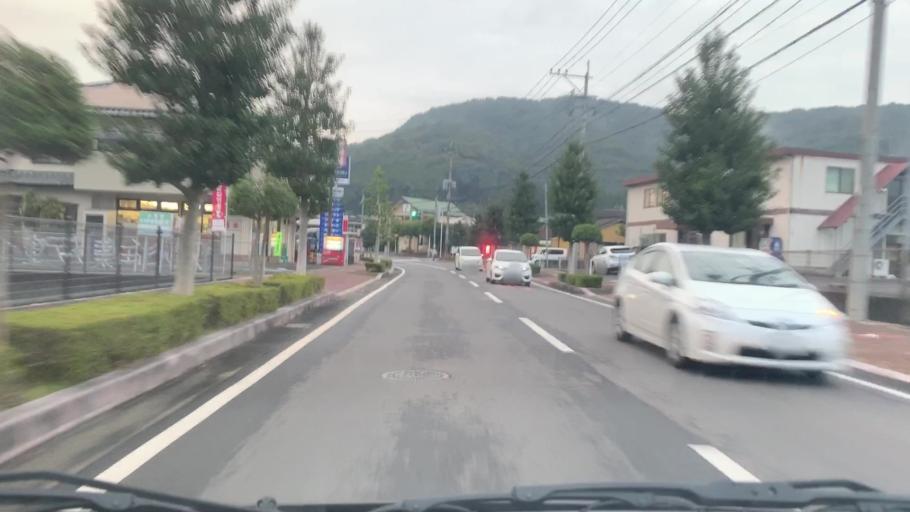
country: JP
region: Saga Prefecture
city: Ureshinomachi-shimojuku
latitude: 33.1490
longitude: 129.9006
